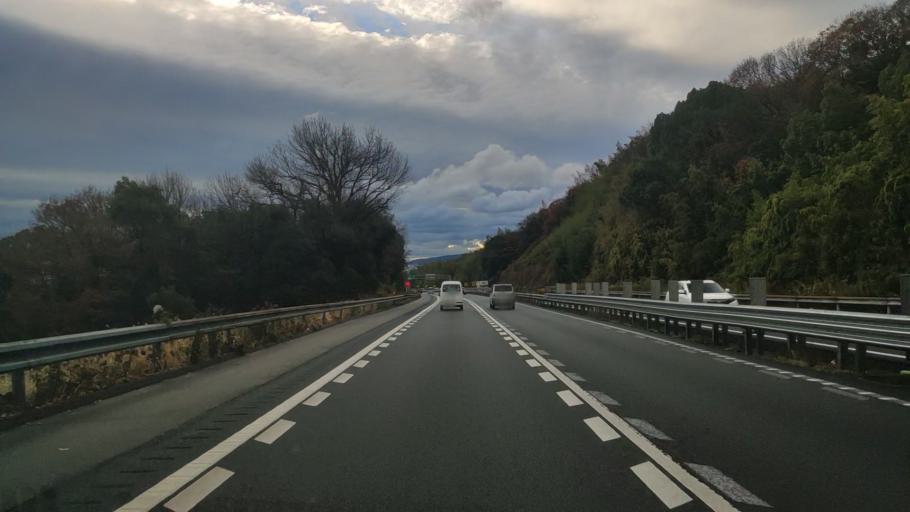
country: JP
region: Hyogo
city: Akashi
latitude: 34.6932
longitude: 134.9694
